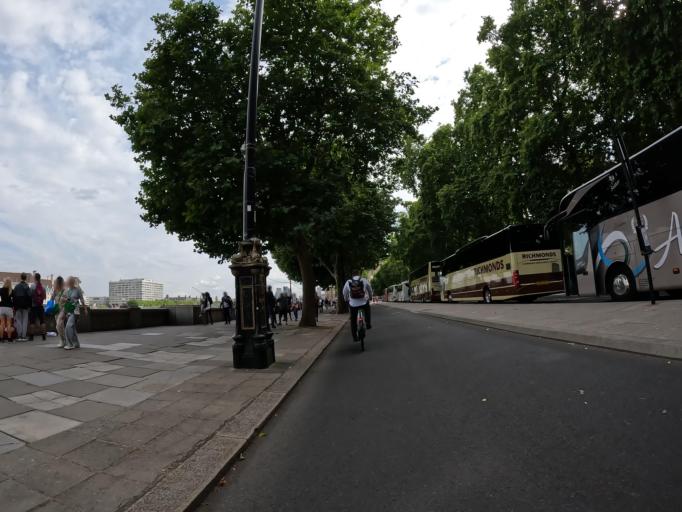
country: GB
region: England
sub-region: Greater London
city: Bromley
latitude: 51.4260
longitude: 0.0167
